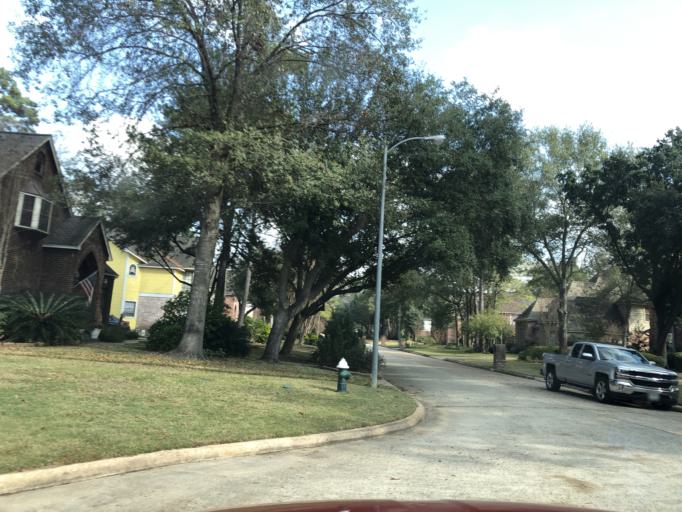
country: US
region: Texas
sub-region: Harris County
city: Tomball
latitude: 30.0290
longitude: -95.5463
